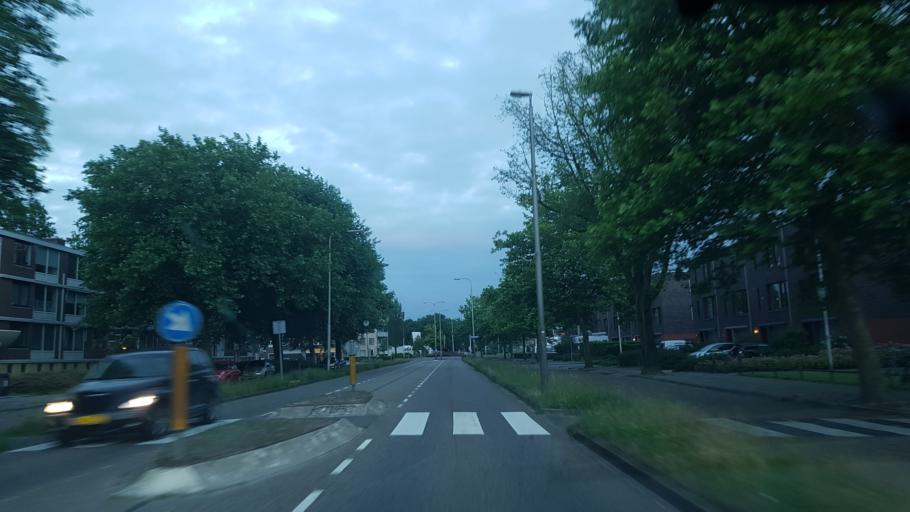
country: NL
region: Friesland
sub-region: Gemeente Leeuwarden
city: Leeuwarden
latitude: 53.2091
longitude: 5.8181
